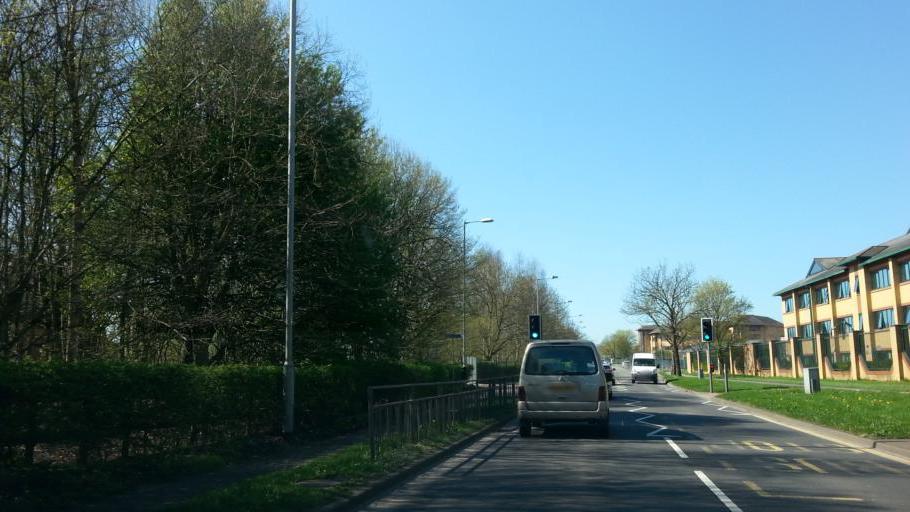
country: GB
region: England
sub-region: Staffordshire
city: Stafford
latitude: 52.8145
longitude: -2.0768
